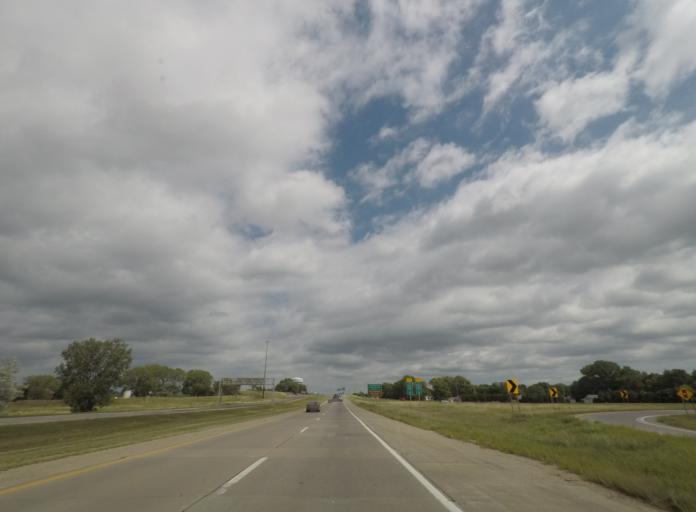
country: US
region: Iowa
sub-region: Linn County
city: Cedar Rapids
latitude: 41.9267
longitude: -91.6555
